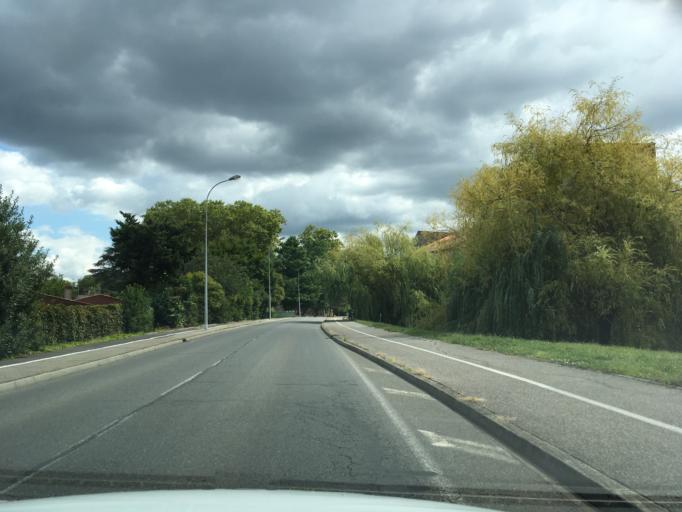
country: FR
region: Aquitaine
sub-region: Departement du Lot-et-Garonne
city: Agen
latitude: 44.2073
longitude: 0.6345
